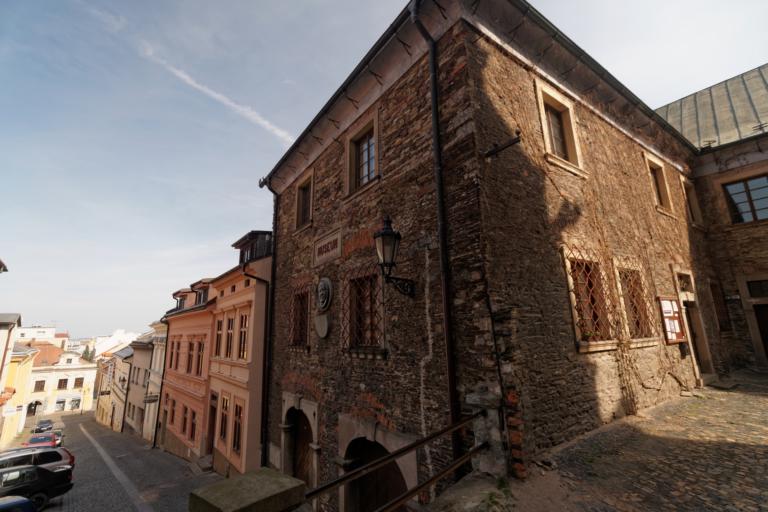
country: CZ
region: Central Bohemia
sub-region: Okres Kolin
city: Kolin
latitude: 50.0267
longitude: 15.2021
